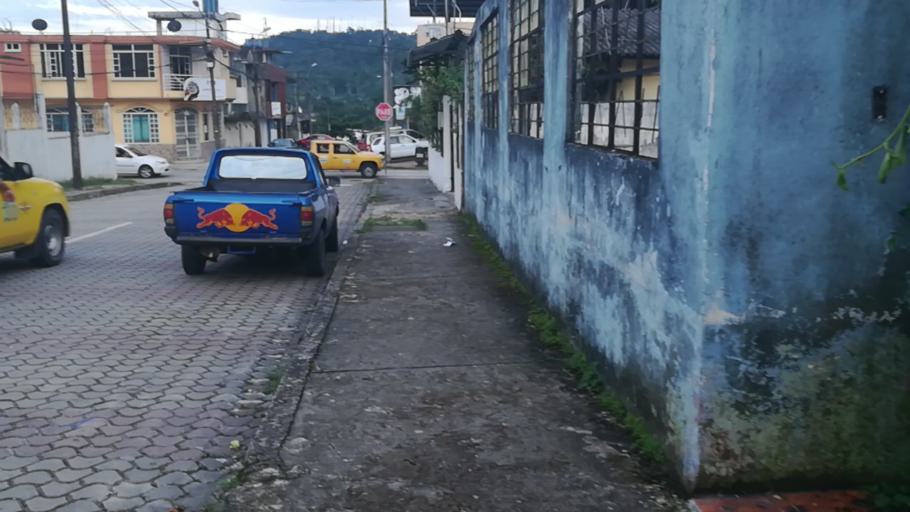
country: EC
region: Napo
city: Tena
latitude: -0.9893
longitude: -77.8154
